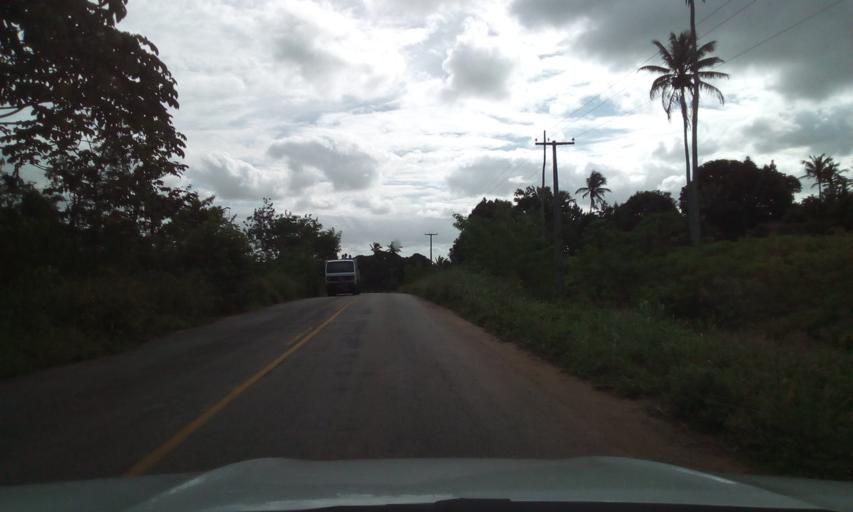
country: BR
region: Paraiba
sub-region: Cabedelo
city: Cabedelo
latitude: -6.9442
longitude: -34.9240
